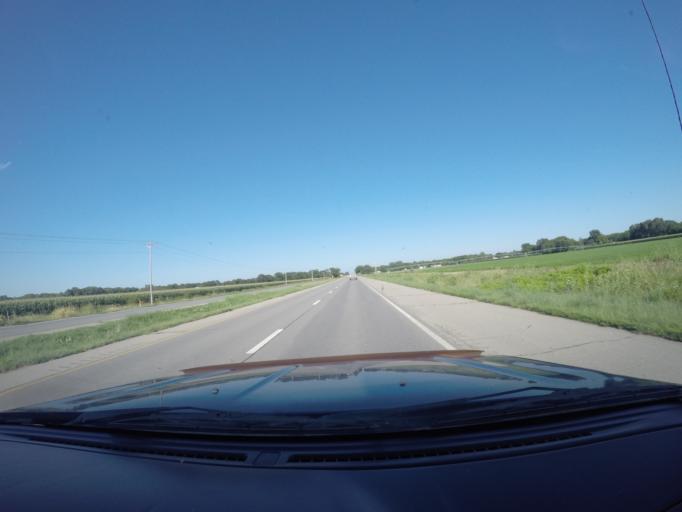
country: US
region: Kansas
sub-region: Shawnee County
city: Topeka
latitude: 39.0875
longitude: -95.5651
